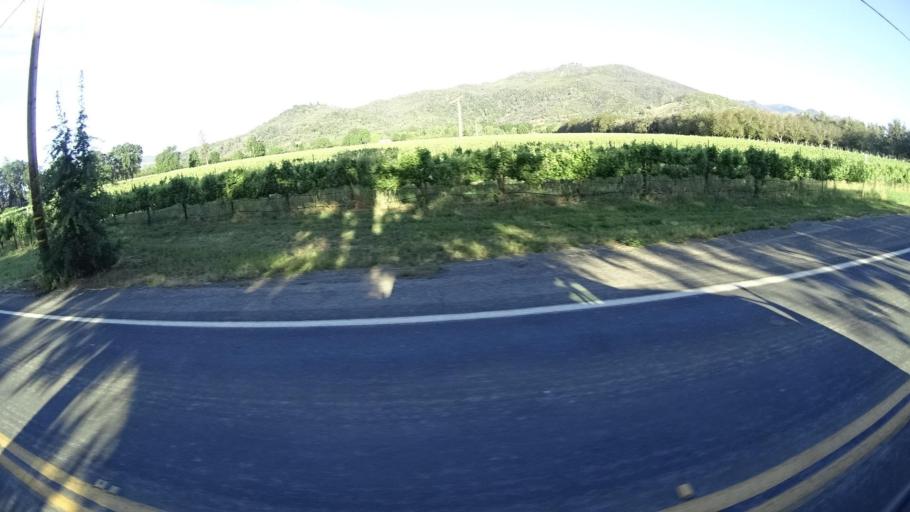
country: US
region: California
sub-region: Lake County
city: Upper Lake
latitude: 39.1876
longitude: -122.9008
